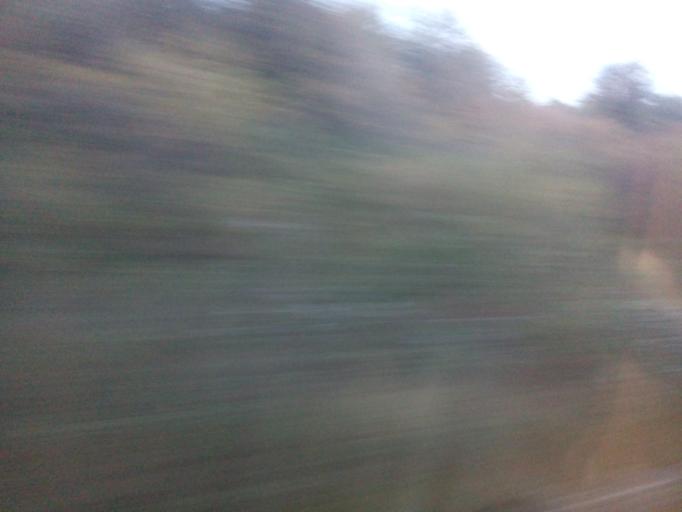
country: GB
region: England
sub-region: Rotherham
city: Rotherham
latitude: 53.4252
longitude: -1.3955
